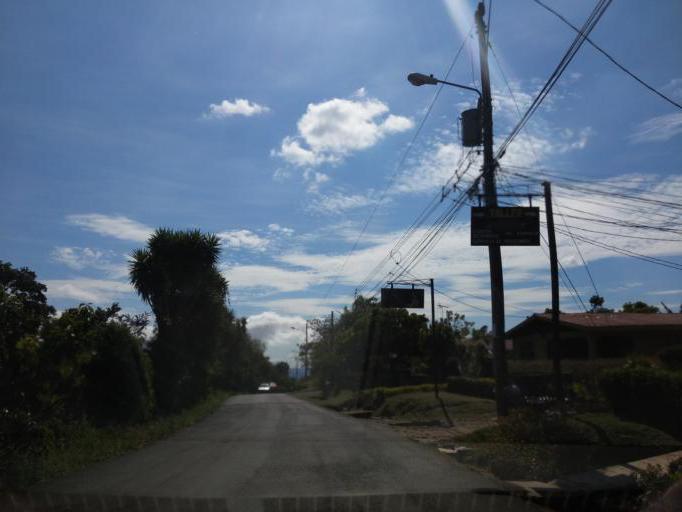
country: CR
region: Heredia
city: Santo Domingo
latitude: 10.0588
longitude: -84.1484
